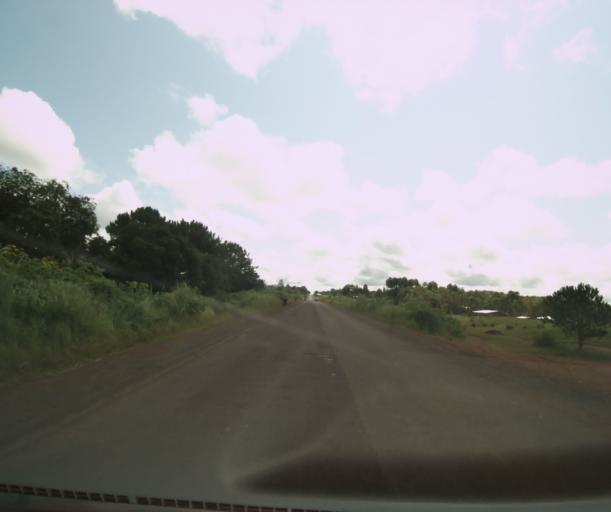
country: CM
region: West
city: Foumban
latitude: 5.6597
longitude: 10.7735
